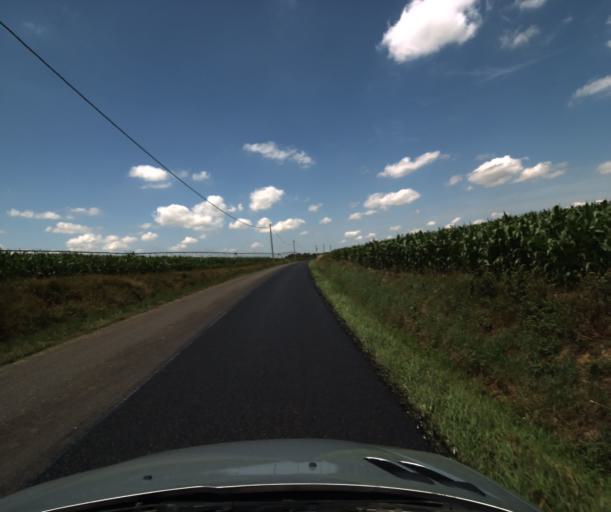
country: FR
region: Midi-Pyrenees
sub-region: Departement de la Haute-Garonne
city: Saint-Lys
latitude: 43.4926
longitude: 1.2063
